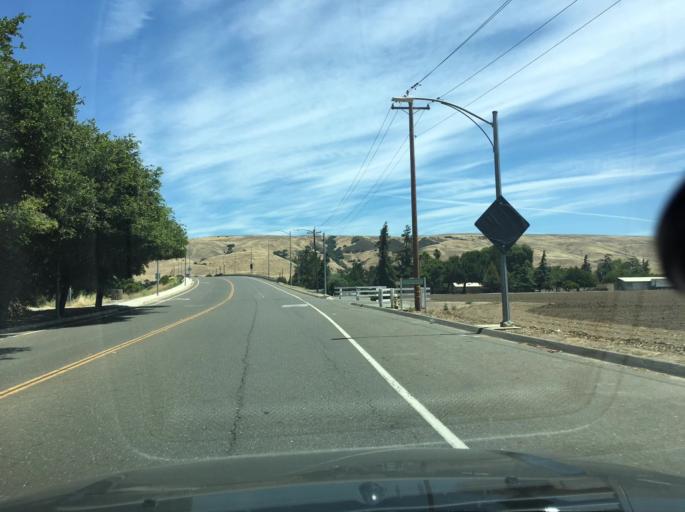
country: US
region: California
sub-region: Santa Clara County
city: Morgan Hill
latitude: 37.2042
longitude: -121.7323
